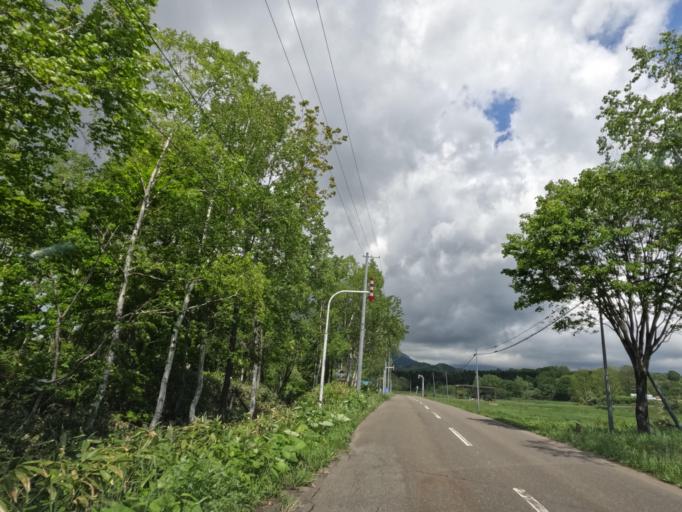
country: JP
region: Hokkaido
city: Tobetsu
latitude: 43.4498
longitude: 141.5869
